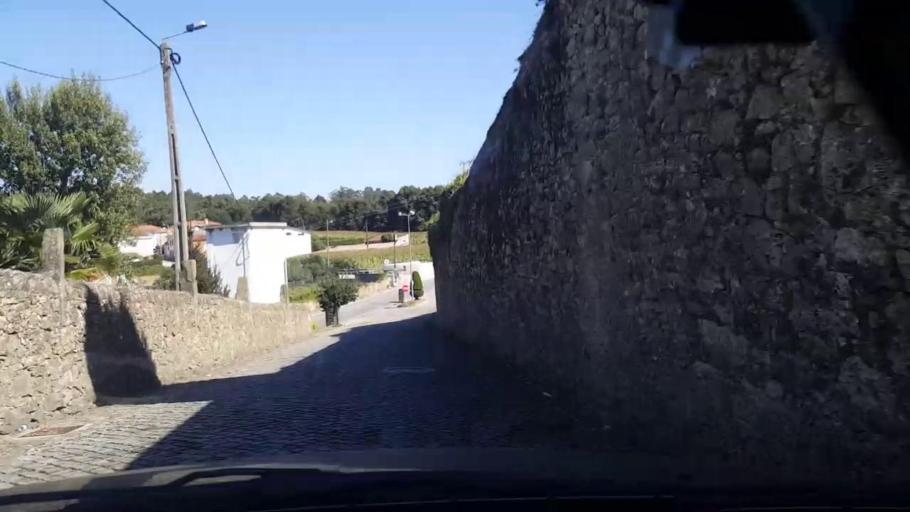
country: PT
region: Porto
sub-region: Vila do Conde
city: Arvore
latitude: 41.3334
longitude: -8.6667
